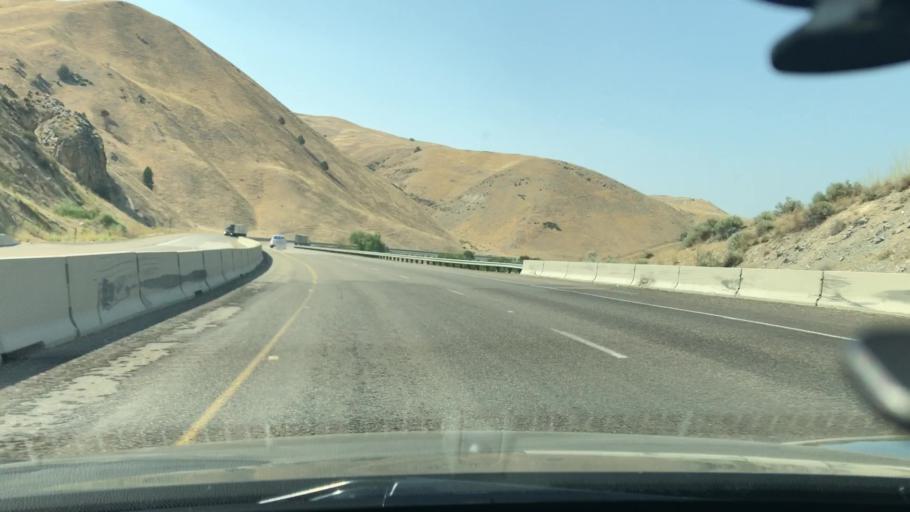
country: US
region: Idaho
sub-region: Washington County
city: Weiser
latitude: 44.4025
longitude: -117.3094
